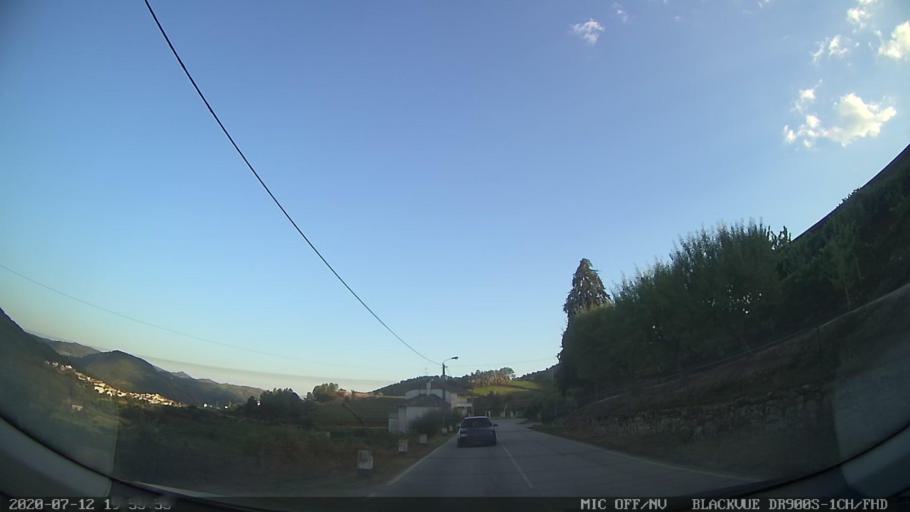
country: PT
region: Viseu
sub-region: Sao Joao da Pesqueira
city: Sao Joao da Pesqueira
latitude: 41.2559
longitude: -7.4404
